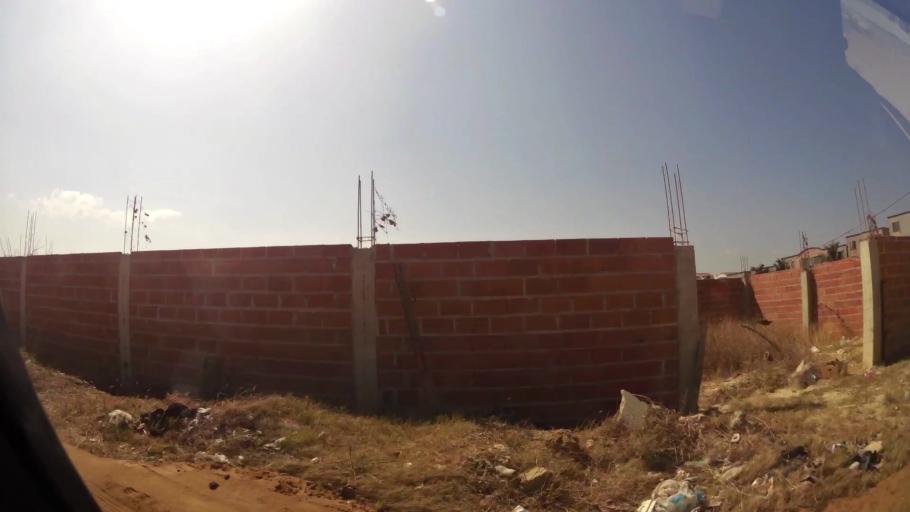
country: CO
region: Atlantico
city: Barranquilla
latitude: 10.9815
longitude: -74.8290
